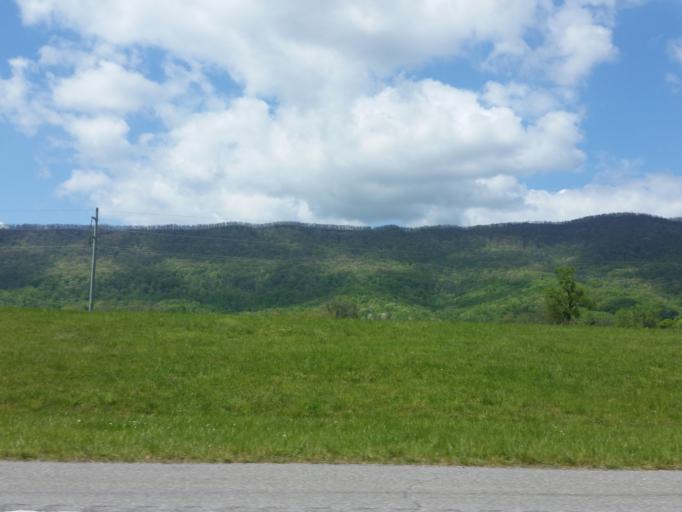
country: US
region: Tennessee
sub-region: Campbell County
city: Fincastle
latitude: 36.4295
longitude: -84.0221
